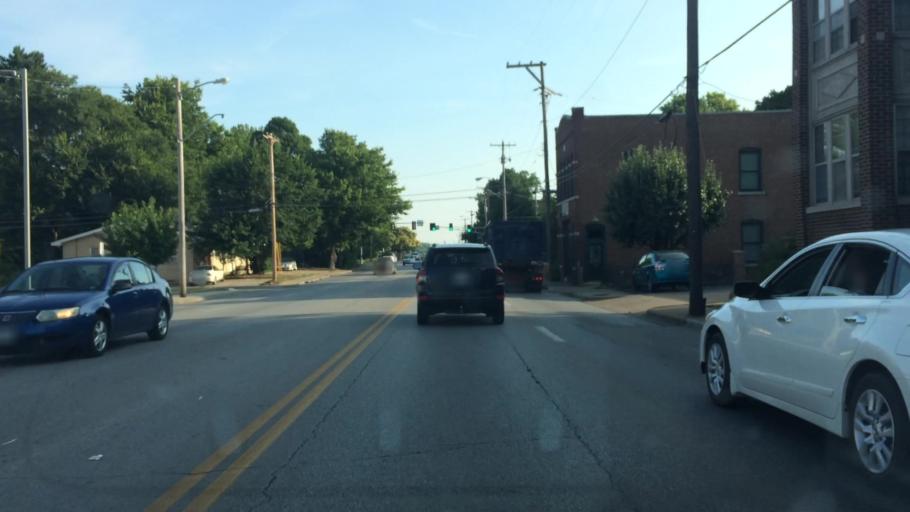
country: US
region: Missouri
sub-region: Greene County
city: Springfield
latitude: 37.2053
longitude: -93.2761
